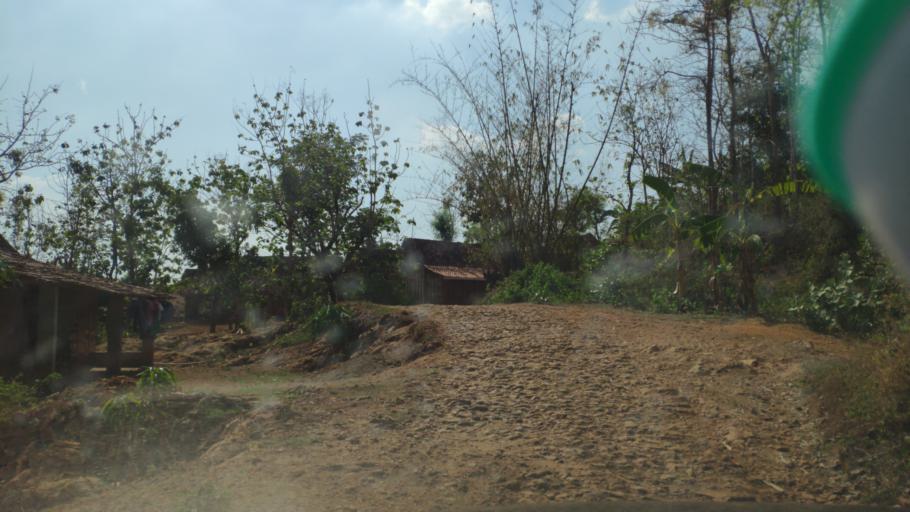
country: ID
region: Central Java
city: Ngapus
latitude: -6.9379
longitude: 111.2119
